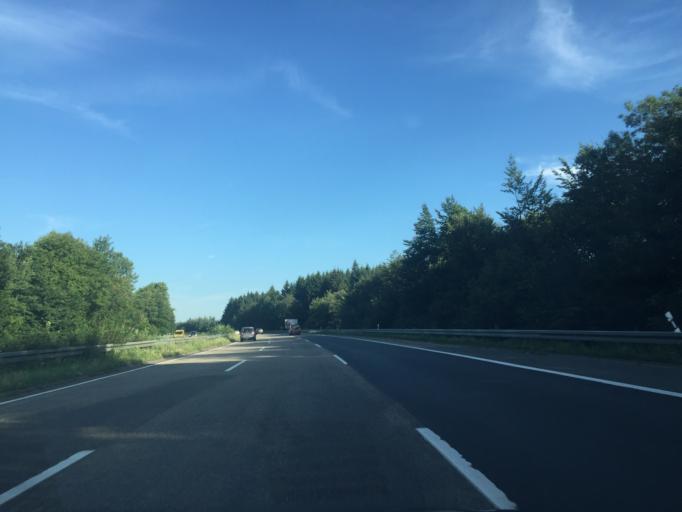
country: DE
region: North Rhine-Westphalia
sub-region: Regierungsbezirk Arnsberg
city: Drolshagen
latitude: 51.0615
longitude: 7.7189
